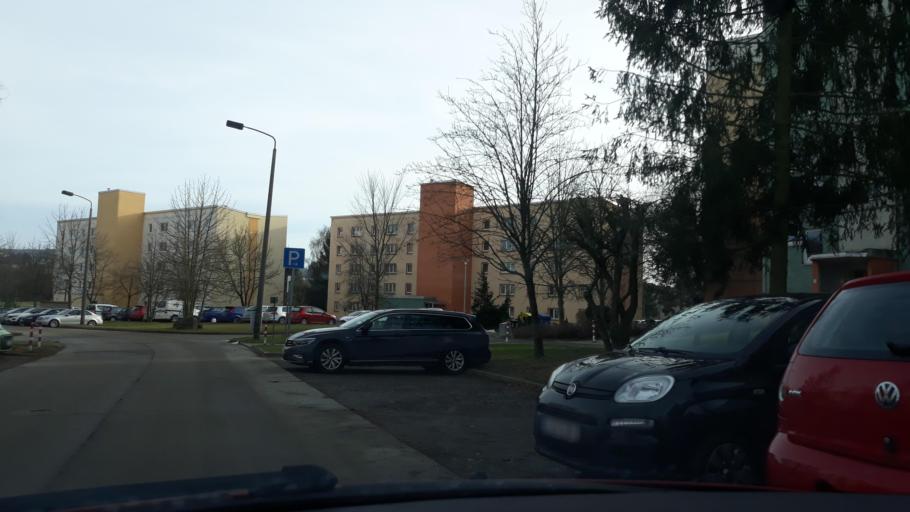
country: DE
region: Saxony
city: Kirchberg
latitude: 50.6168
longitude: 12.5152
